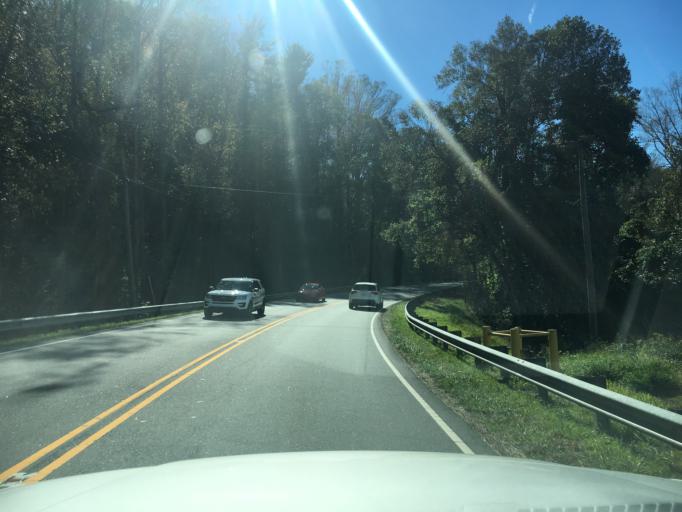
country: US
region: North Carolina
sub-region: Burke County
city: Morganton
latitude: 35.7468
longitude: -81.7045
